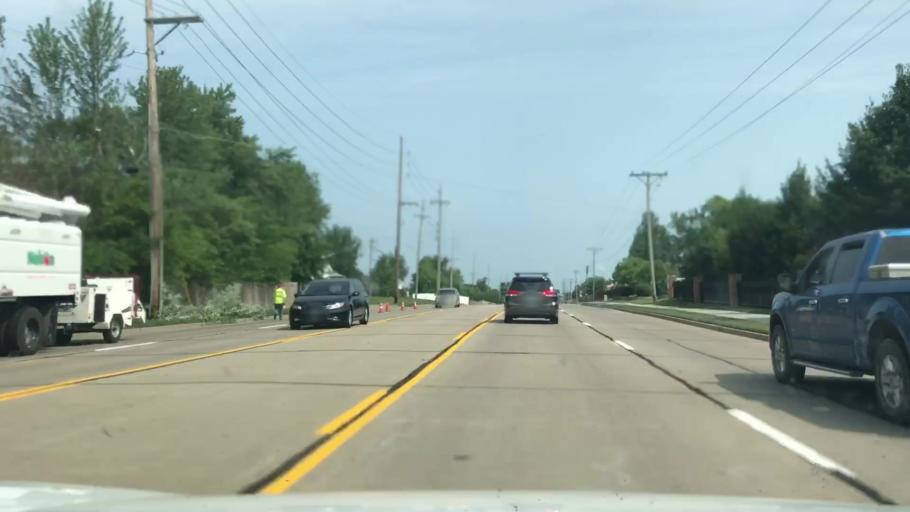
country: US
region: Missouri
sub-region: Saint Charles County
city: Dardenne Prairie
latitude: 38.7794
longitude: -90.7374
